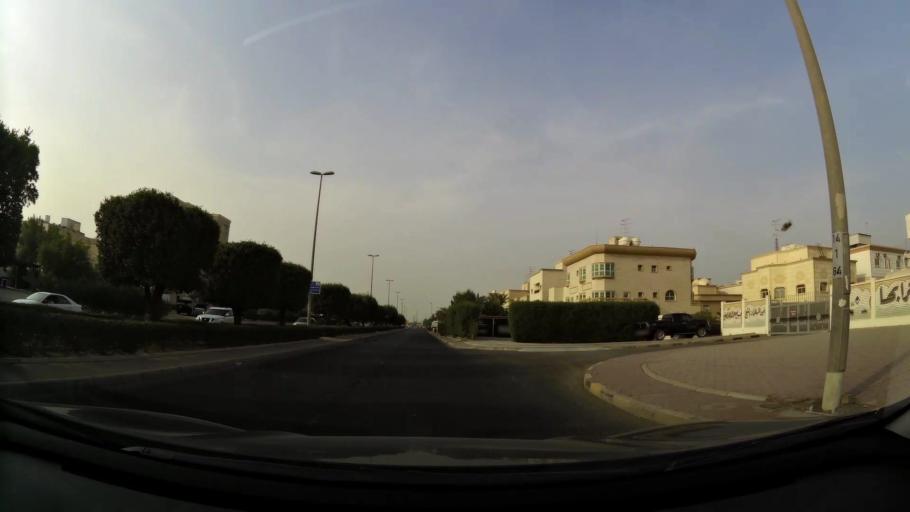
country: KW
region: Mubarak al Kabir
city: Mubarak al Kabir
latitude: 29.1949
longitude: 48.0809
